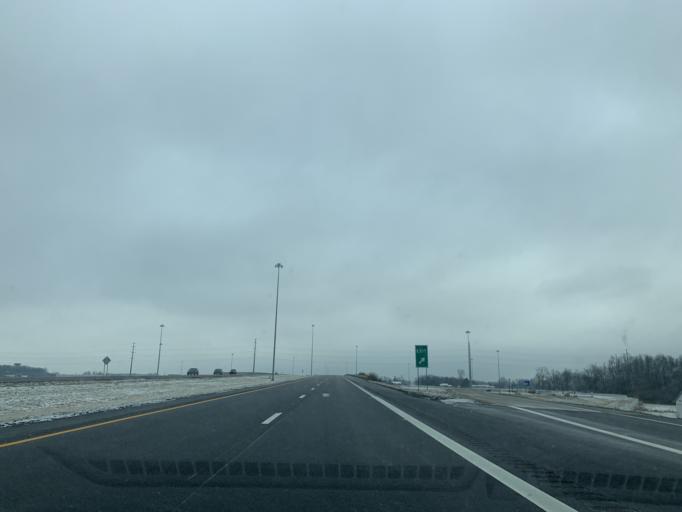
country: US
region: Ohio
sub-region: Franklin County
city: New Albany
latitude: 40.0797
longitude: -82.7588
